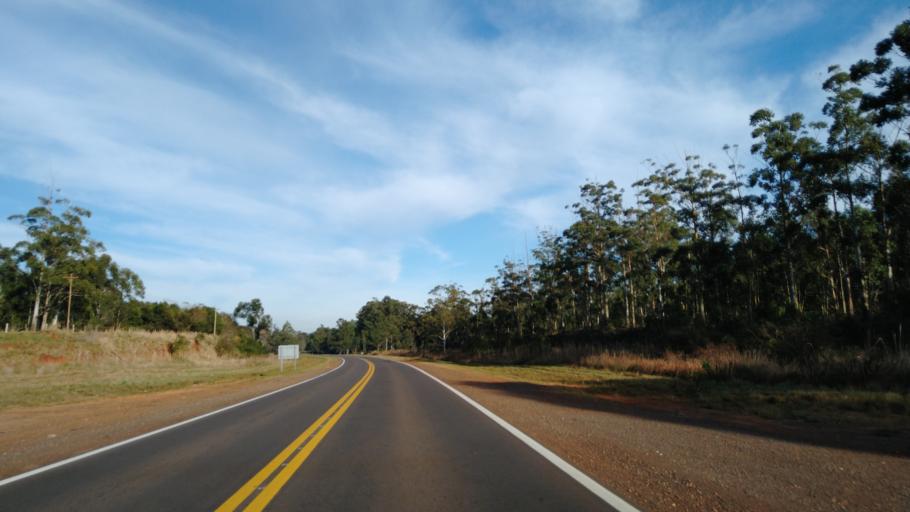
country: AR
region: Corrientes
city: Yapeyu
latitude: -29.4244
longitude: -56.8585
